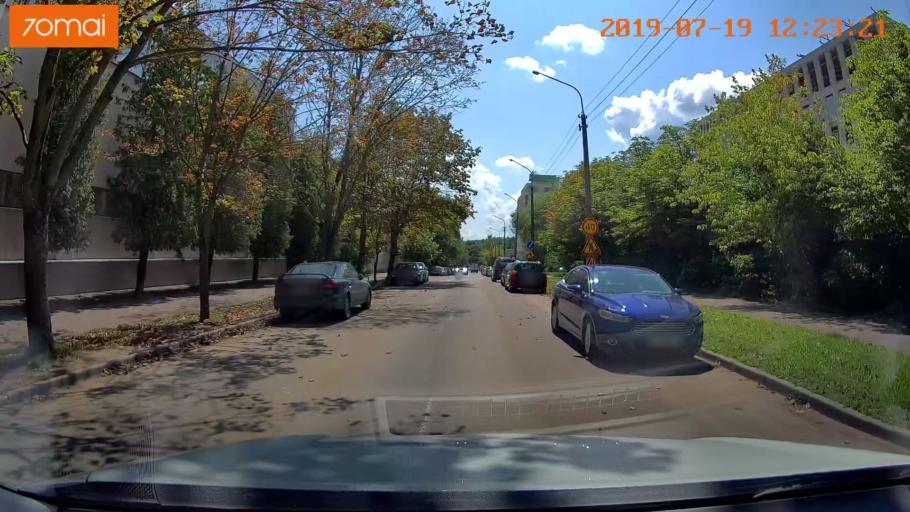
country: BY
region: Minsk
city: Minsk
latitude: 53.9283
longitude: 27.6177
